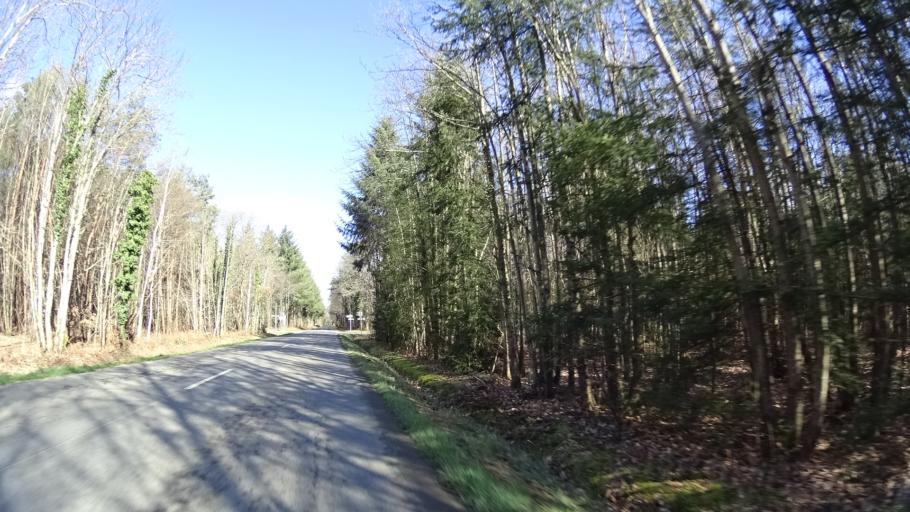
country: FR
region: Brittany
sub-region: Departement d'Ille-et-Vilaine
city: Pleugueneuc
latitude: 48.3560
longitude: -1.9180
